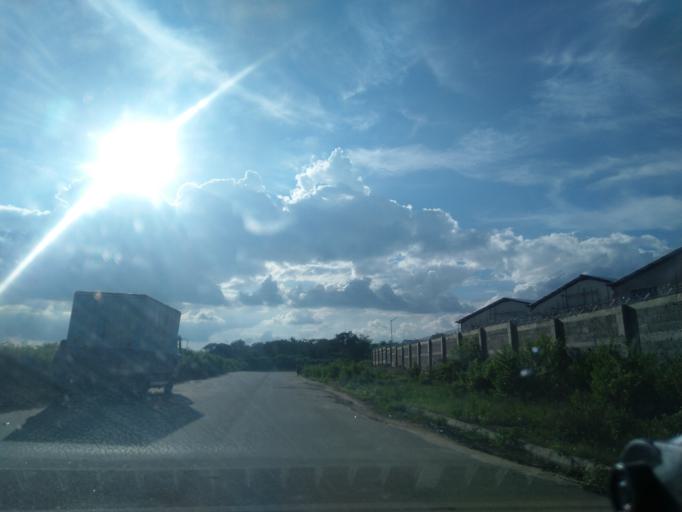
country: NG
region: Abuja Federal Capital Territory
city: Abuja
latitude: 9.0300
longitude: 7.3998
